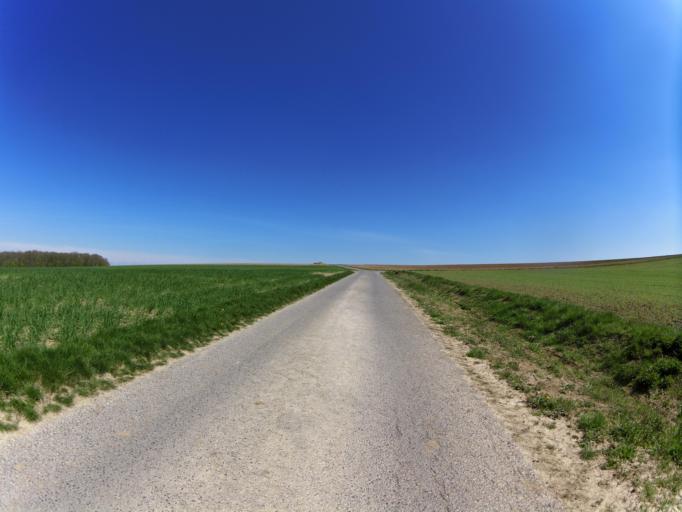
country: DE
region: Bavaria
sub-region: Regierungsbezirk Unterfranken
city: Winterhausen
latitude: 49.6895
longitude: 9.9990
